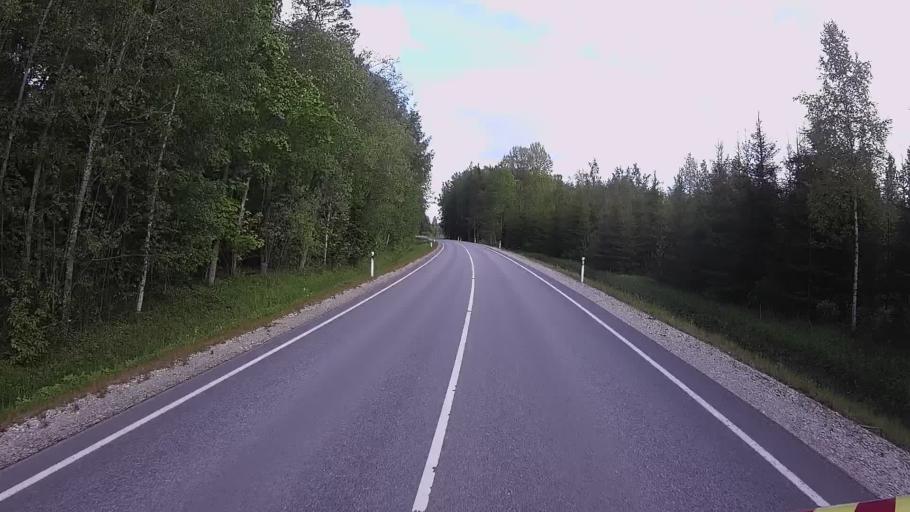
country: EE
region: Jogevamaa
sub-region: Mustvee linn
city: Mustvee
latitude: 58.8714
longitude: 26.8243
